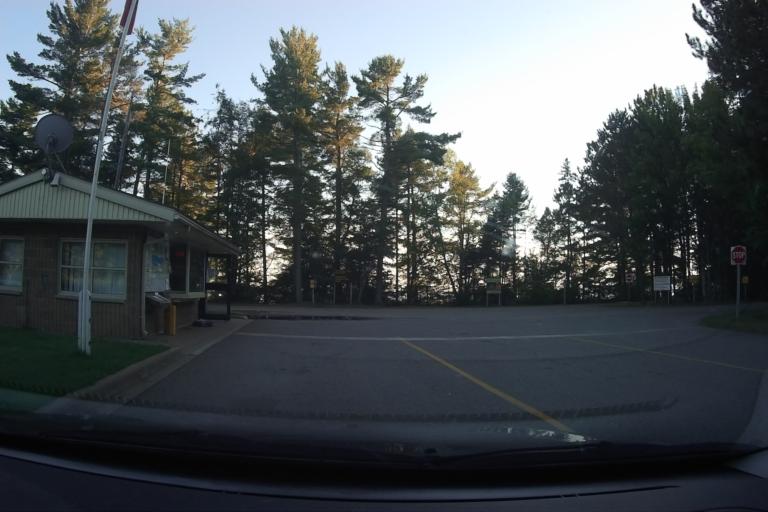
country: CA
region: Ontario
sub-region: Algoma
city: Sault Ste. Marie
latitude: 46.9684
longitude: -84.6816
